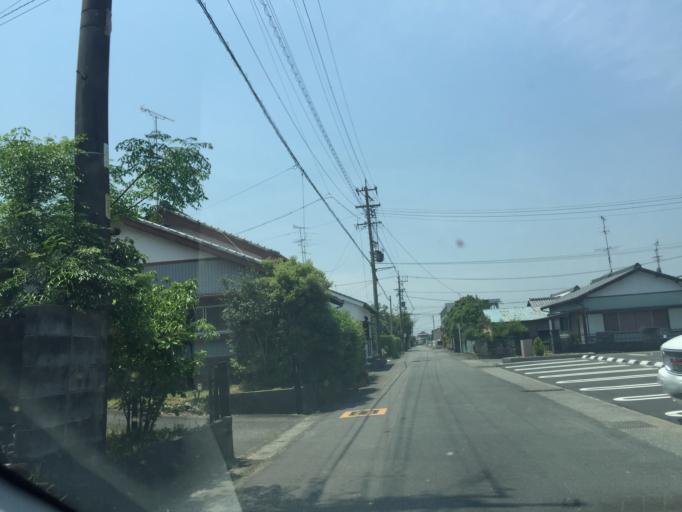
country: JP
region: Shizuoka
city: Kakegawa
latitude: 34.7709
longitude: 137.9902
